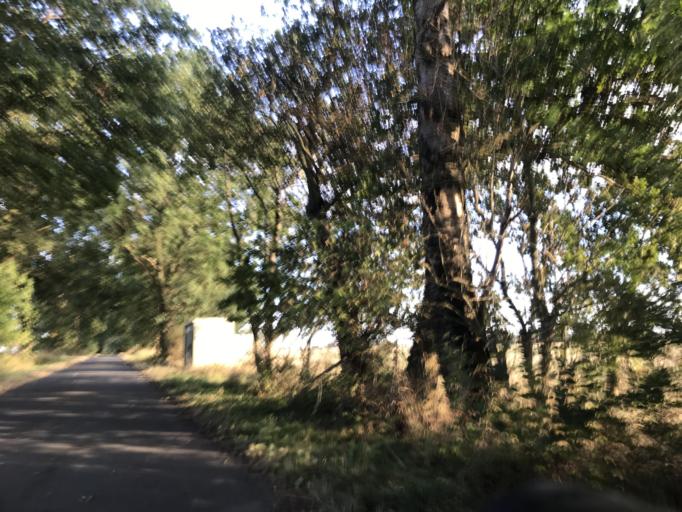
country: DE
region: Lower Saxony
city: Reinstorf
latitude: 53.2322
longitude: 10.5966
